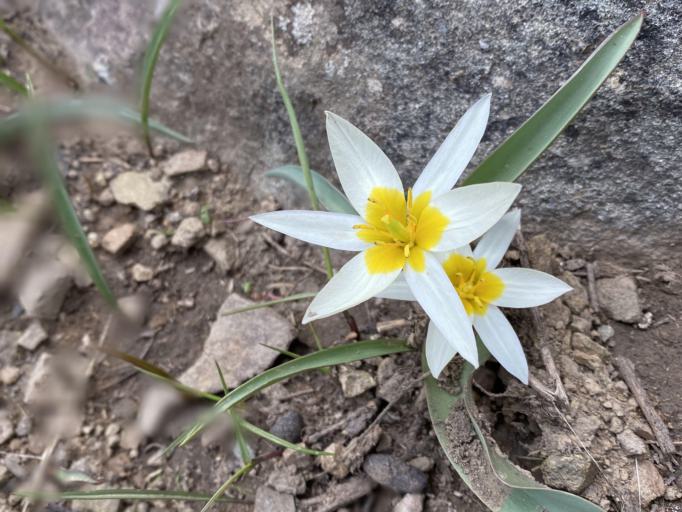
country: KZ
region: Ongtustik Qazaqstan
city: Kentau
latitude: 43.8405
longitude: 68.4992
